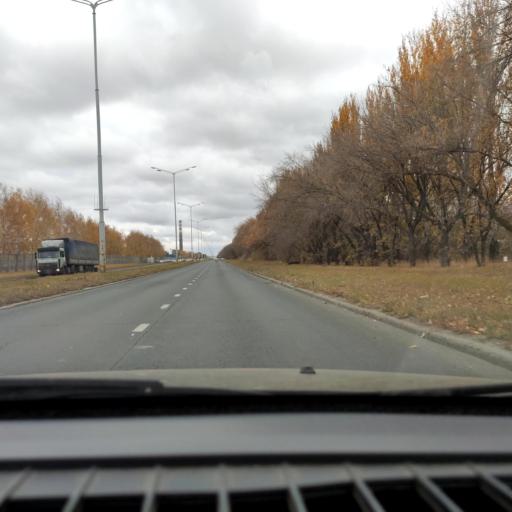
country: RU
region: Samara
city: Tol'yatti
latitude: 53.5683
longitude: 49.2730
